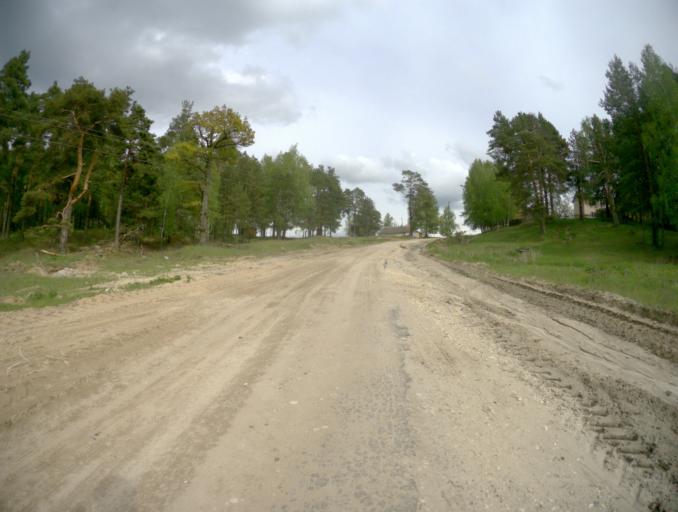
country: RU
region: Rjazan
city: Gus'-Zheleznyy
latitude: 55.0074
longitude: 41.1936
